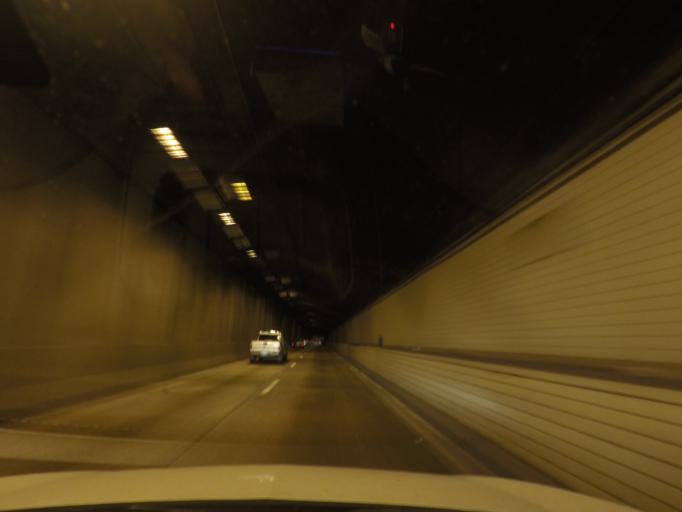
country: BR
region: Rio de Janeiro
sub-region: Rio De Janeiro
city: Rio de Janeiro
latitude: -22.9302
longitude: -43.1863
